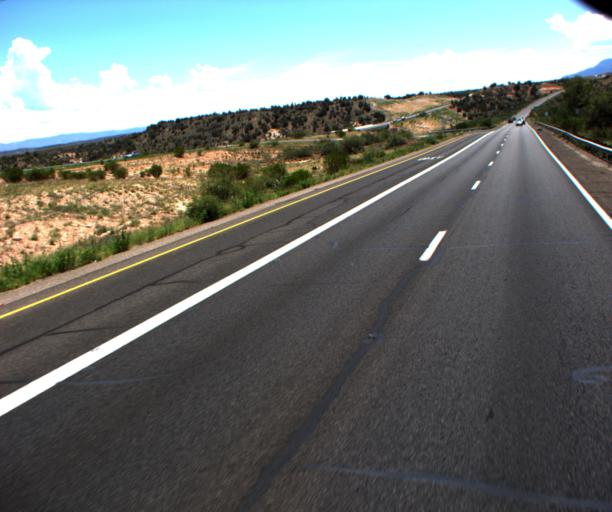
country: US
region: Arizona
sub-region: Yavapai County
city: Verde Village
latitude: 34.6813
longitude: -111.9755
